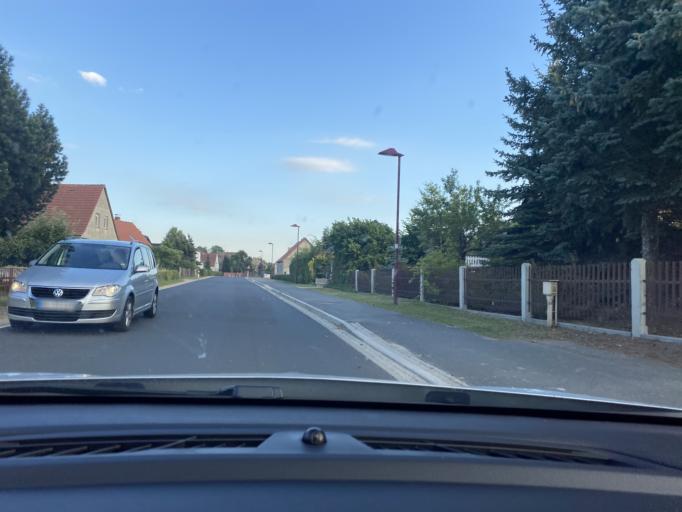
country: DE
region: Saxony
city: Kodersdorf
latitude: 51.2656
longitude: 14.8844
